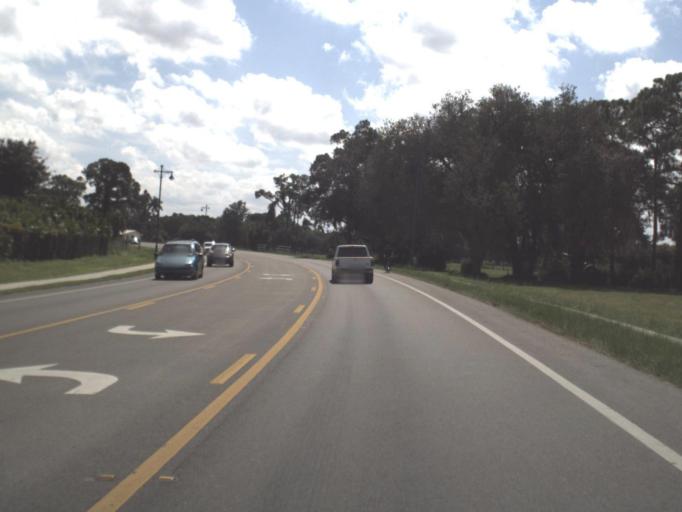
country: US
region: Florida
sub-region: Collier County
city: Immokalee
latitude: 26.4213
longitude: -81.4333
